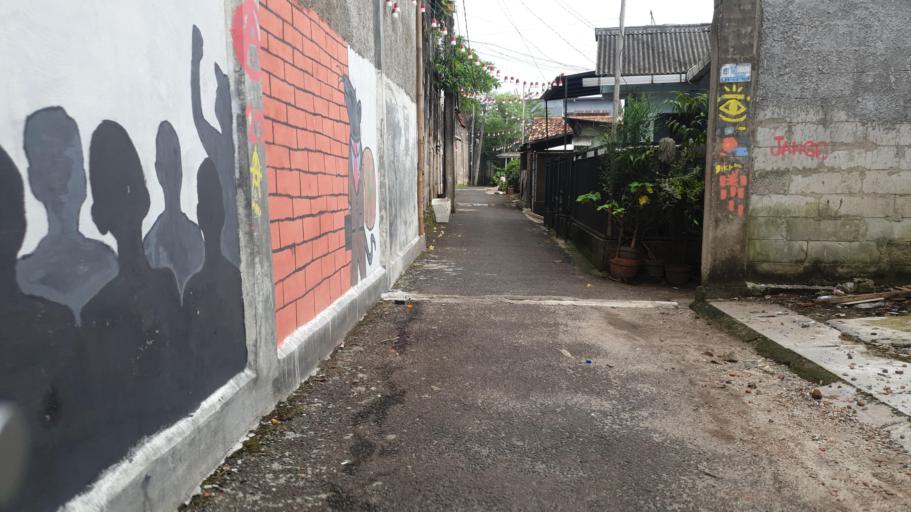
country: ID
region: West Java
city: Pamulang
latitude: -6.3034
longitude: 106.7865
